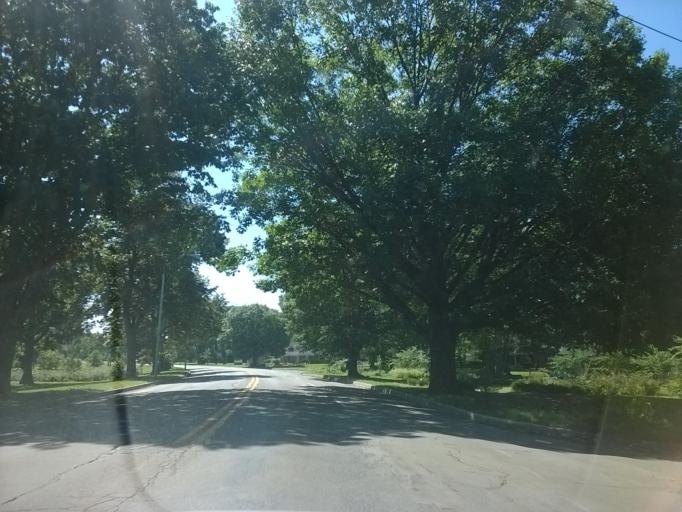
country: US
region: Indiana
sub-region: Marion County
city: Indianapolis
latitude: 39.8011
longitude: -86.1638
